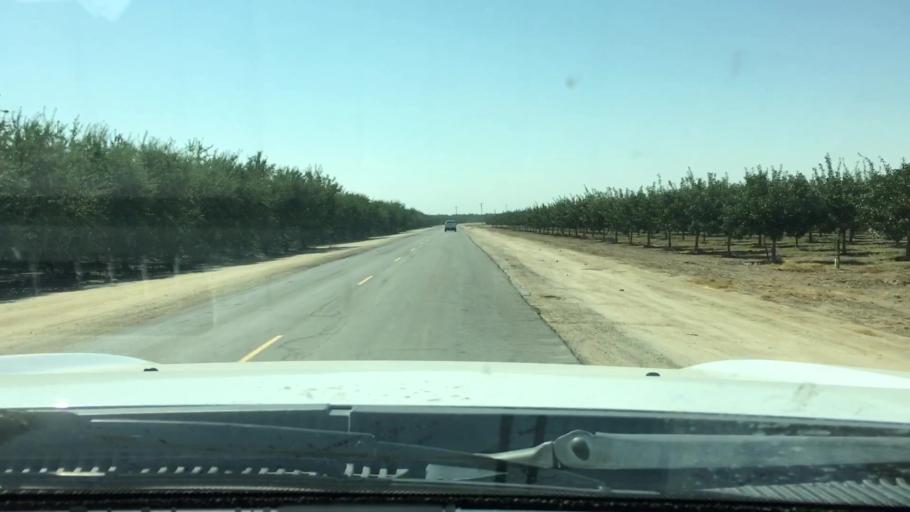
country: US
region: California
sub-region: Kern County
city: Shafter
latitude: 35.5557
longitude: -119.2772
